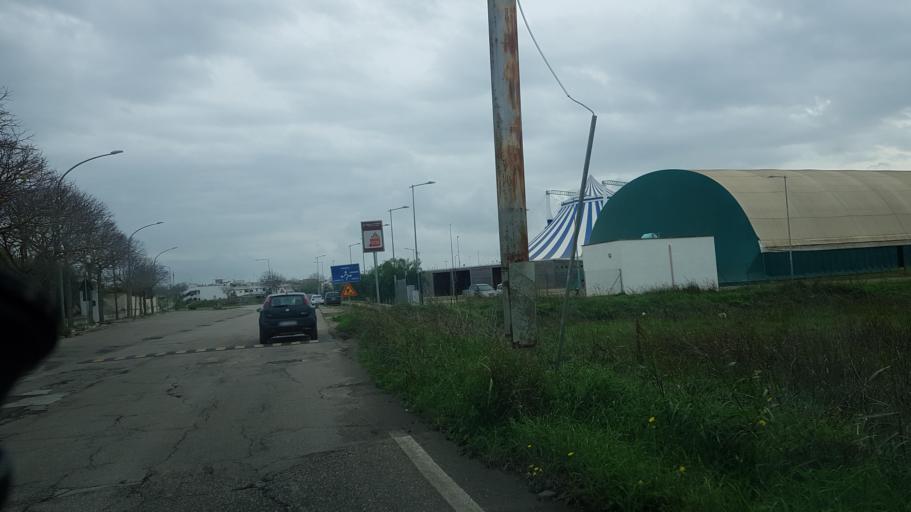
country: IT
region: Apulia
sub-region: Provincia di Lecce
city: Novoli
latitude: 40.3786
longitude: 18.0409
